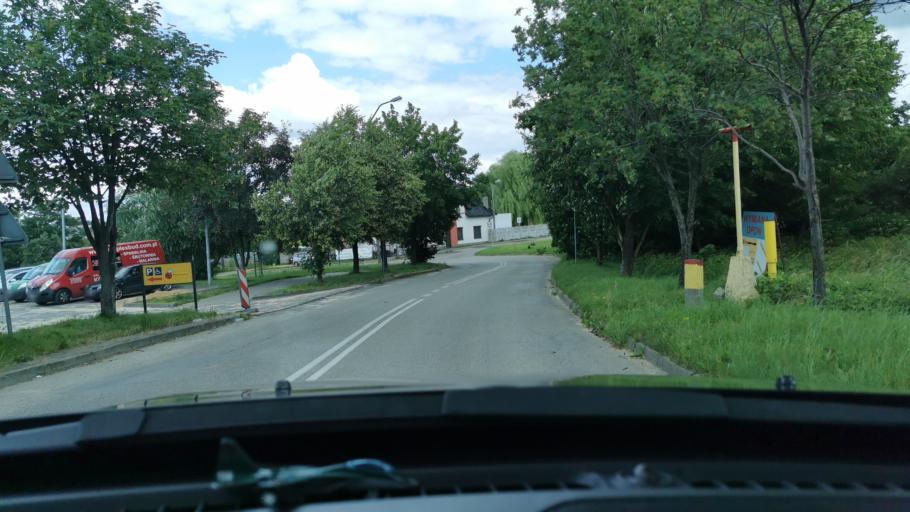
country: PL
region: Lesser Poland Voivodeship
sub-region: Powiat chrzanowski
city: Chrzanow
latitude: 50.1322
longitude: 19.4133
